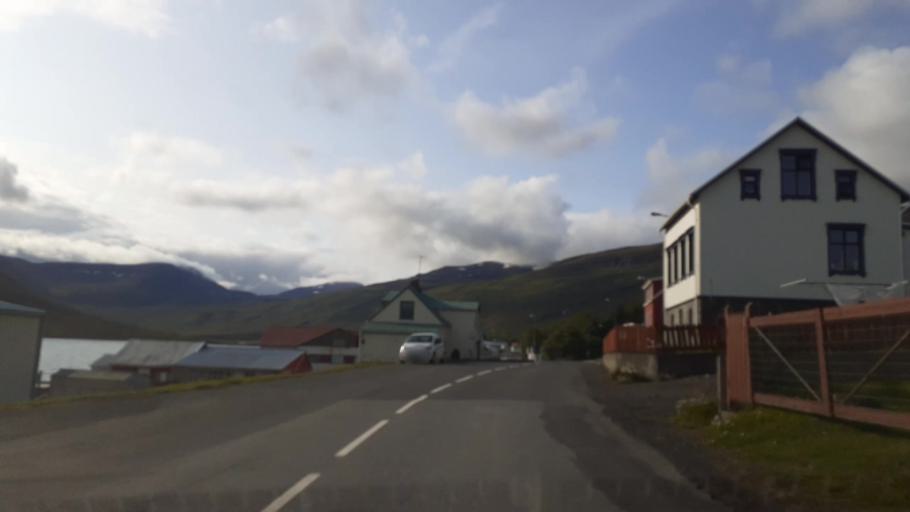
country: IS
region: East
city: Eskifjoerdur
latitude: 65.0653
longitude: -14.0018
